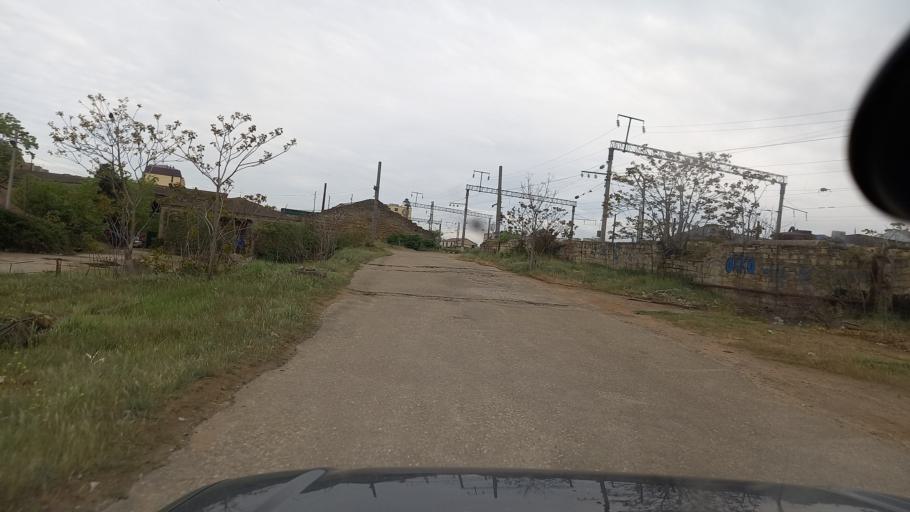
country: RU
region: Dagestan
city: Derbent
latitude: 42.0623
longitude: 48.3052
